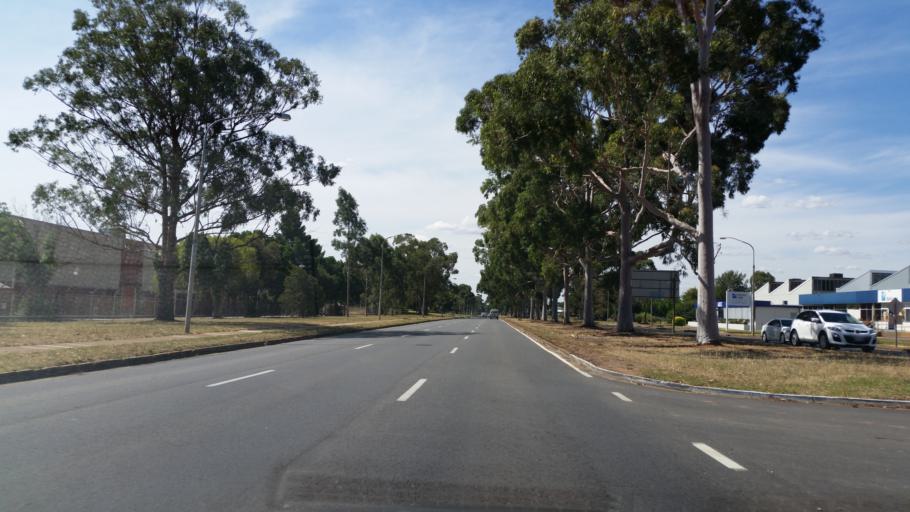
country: AU
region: South Australia
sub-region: Salisbury
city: Salisbury
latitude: -34.7490
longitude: 138.6574
